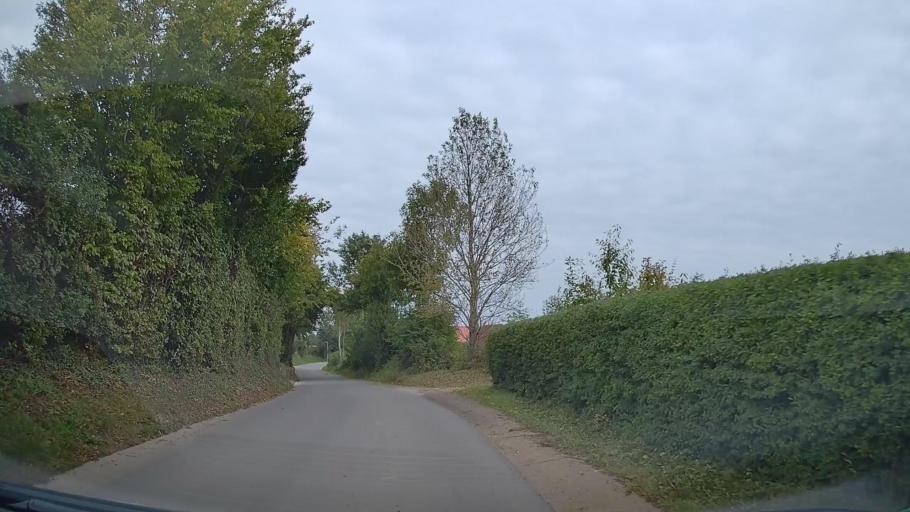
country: DE
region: Schleswig-Holstein
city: Hohenfelde
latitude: 54.3712
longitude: 10.5143
